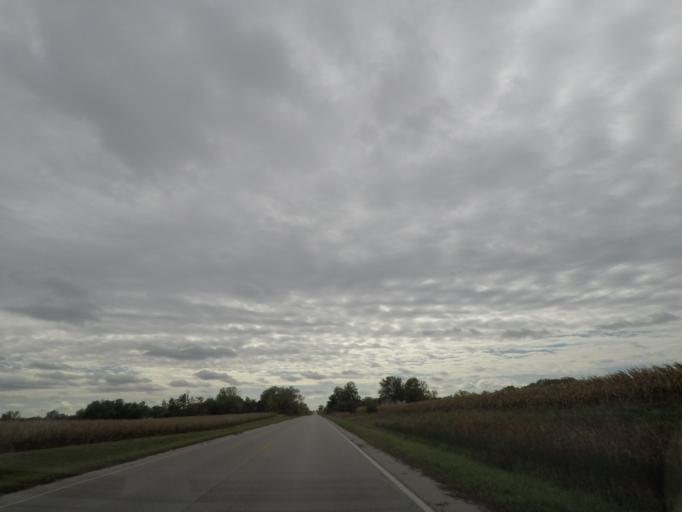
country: US
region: Iowa
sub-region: Story County
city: Huxley
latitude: 41.8724
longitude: -93.5315
